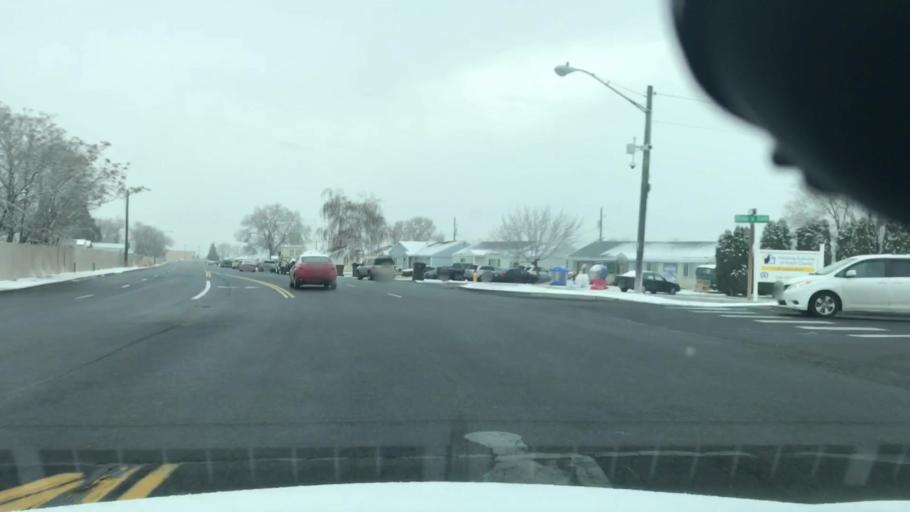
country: US
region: Washington
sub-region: Grant County
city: Moses Lake North
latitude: 47.1784
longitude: -119.3226
